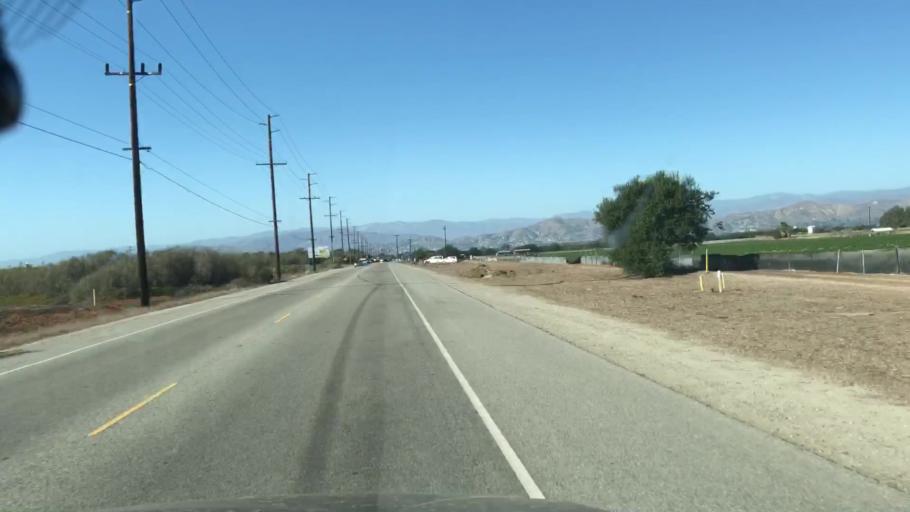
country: US
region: California
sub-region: Ventura County
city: Oxnard Shores
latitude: 34.2157
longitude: -119.2511
